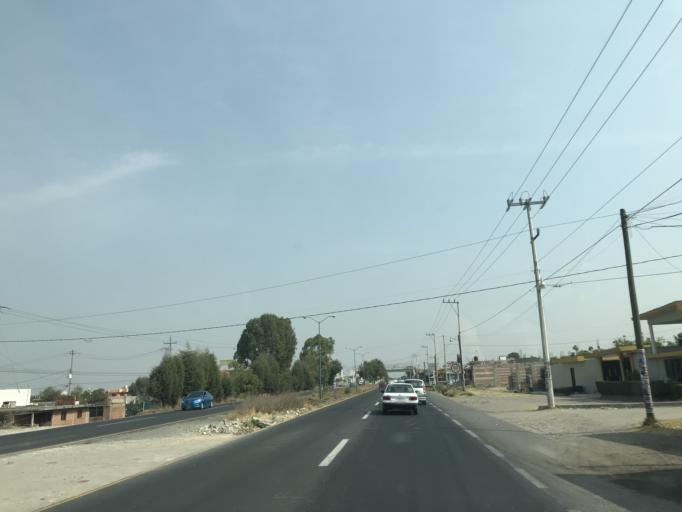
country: MX
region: Tlaxcala
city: Tenancingo
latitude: 19.1457
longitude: -98.1921
